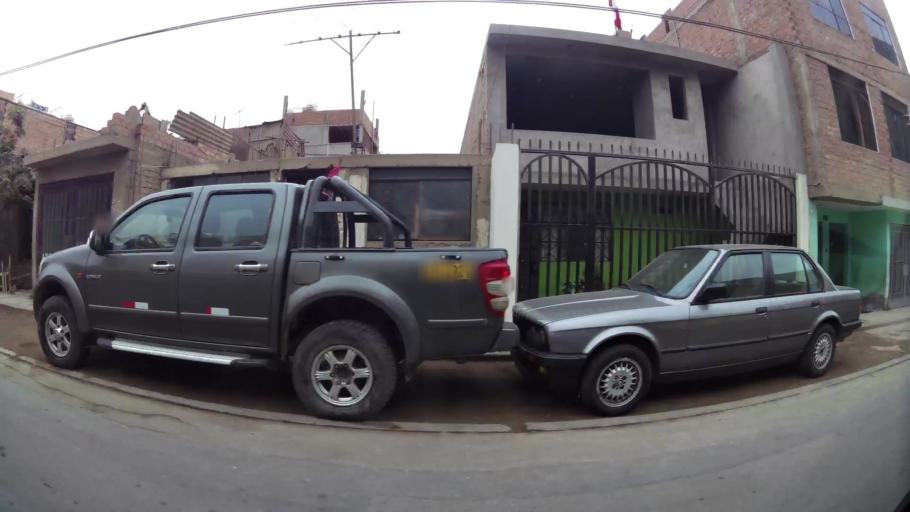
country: PE
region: Lima
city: Ventanilla
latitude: -11.9325
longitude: -77.0860
